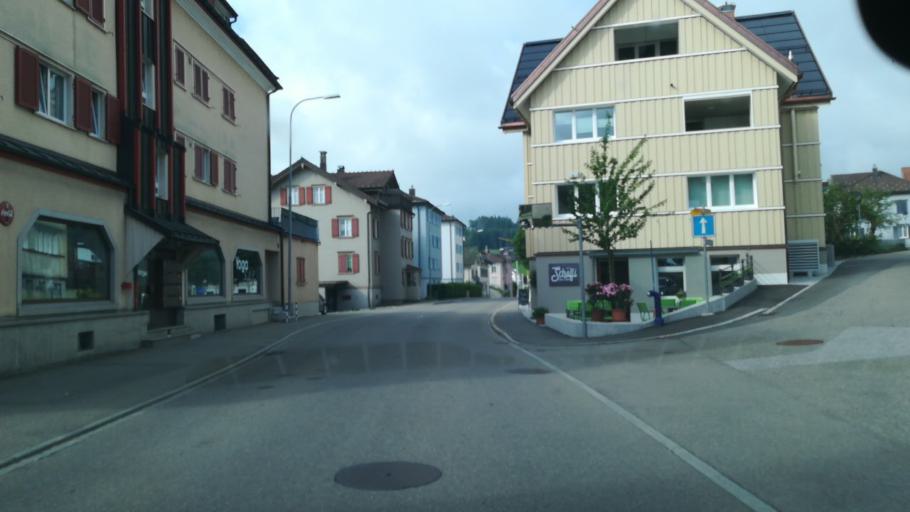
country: CH
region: Appenzell Ausserrhoden
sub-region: Bezirk Hinterland
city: Waldstatt
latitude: 47.3572
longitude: 9.2853
